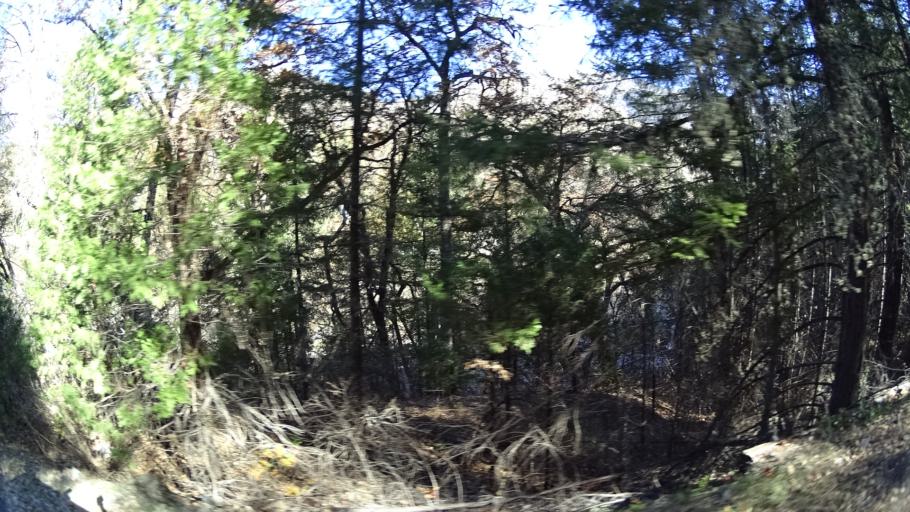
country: US
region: California
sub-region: Siskiyou County
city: Yreka
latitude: 41.8647
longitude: -122.8024
